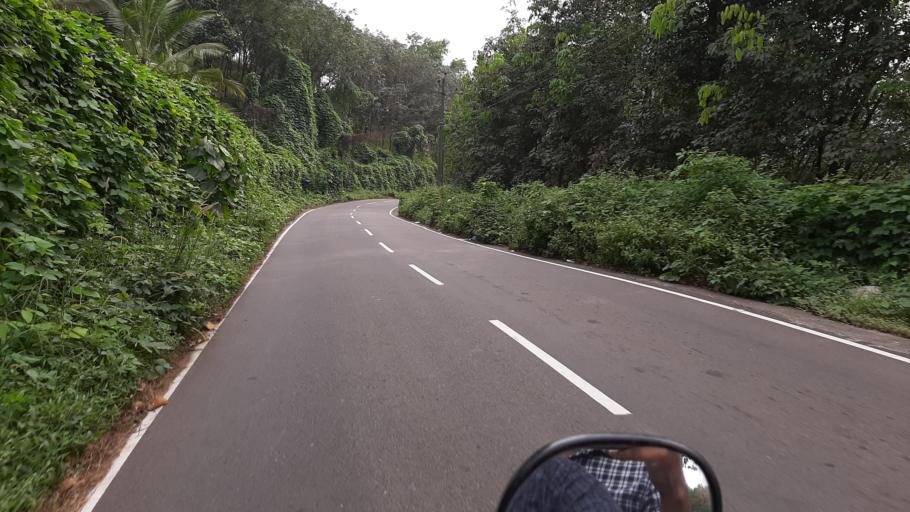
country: IN
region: Kerala
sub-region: Pattanamtitta
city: Pathanamthitta
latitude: 9.4572
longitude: 76.8681
